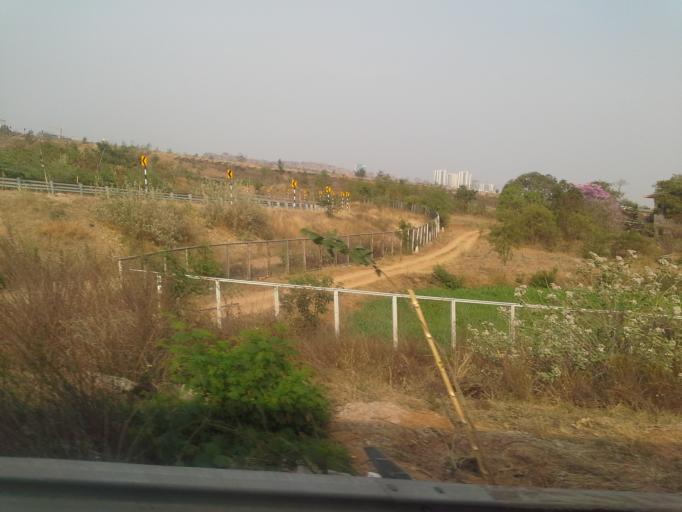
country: IN
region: Telangana
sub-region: Hyderabad
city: Hyderabad
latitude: 17.3943
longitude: 78.3497
